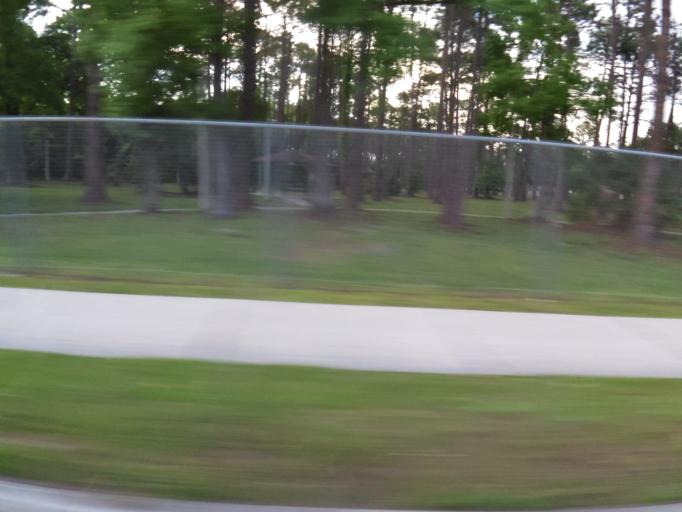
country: US
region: Florida
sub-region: Duval County
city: Jacksonville
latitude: 30.2703
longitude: -81.5995
